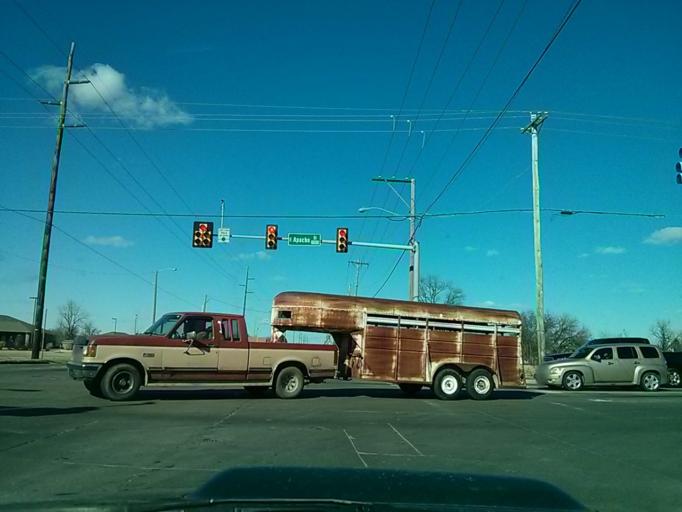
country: US
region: Oklahoma
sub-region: Tulsa County
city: Tulsa
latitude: 36.1916
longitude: -95.9582
